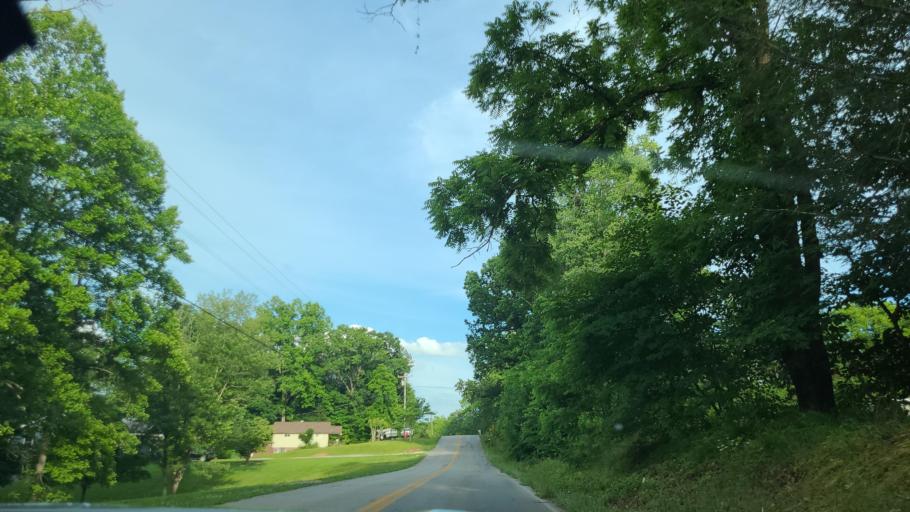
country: US
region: Kentucky
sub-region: Whitley County
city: Corbin
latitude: 36.9127
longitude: -84.2524
